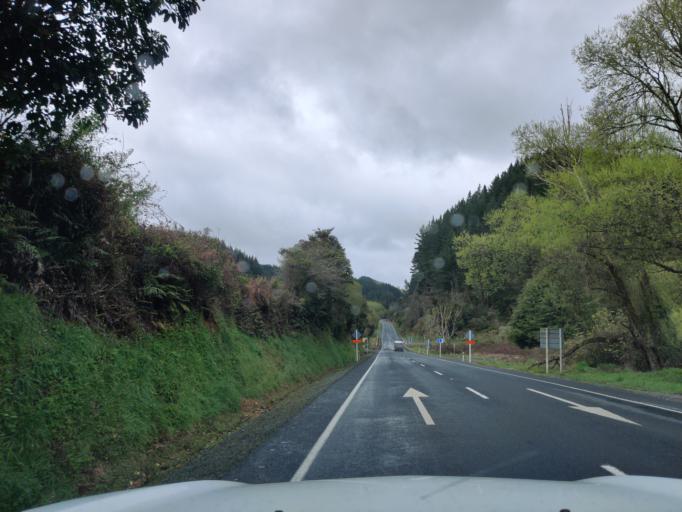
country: NZ
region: Waikato
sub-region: Otorohanga District
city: Otorohanga
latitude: -38.6522
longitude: 175.2078
